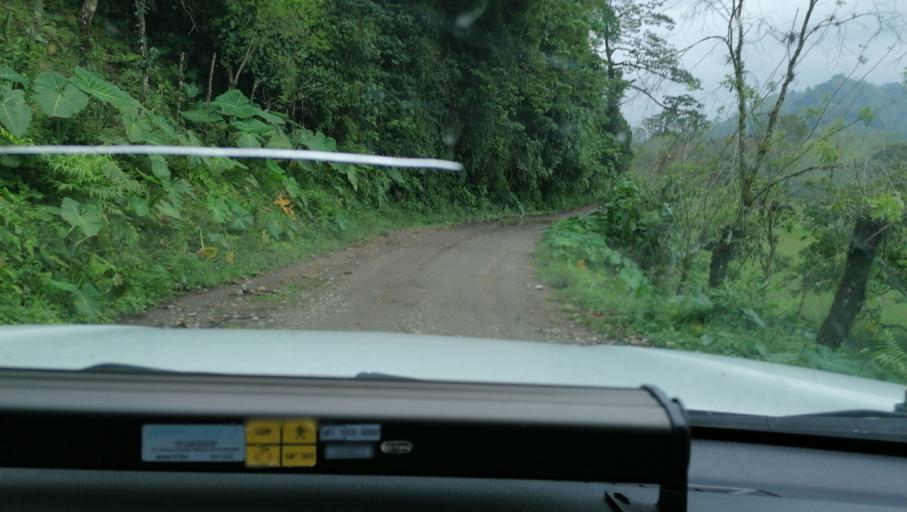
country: MX
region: Chiapas
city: Ixtacomitan
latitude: 17.3547
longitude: -93.1648
